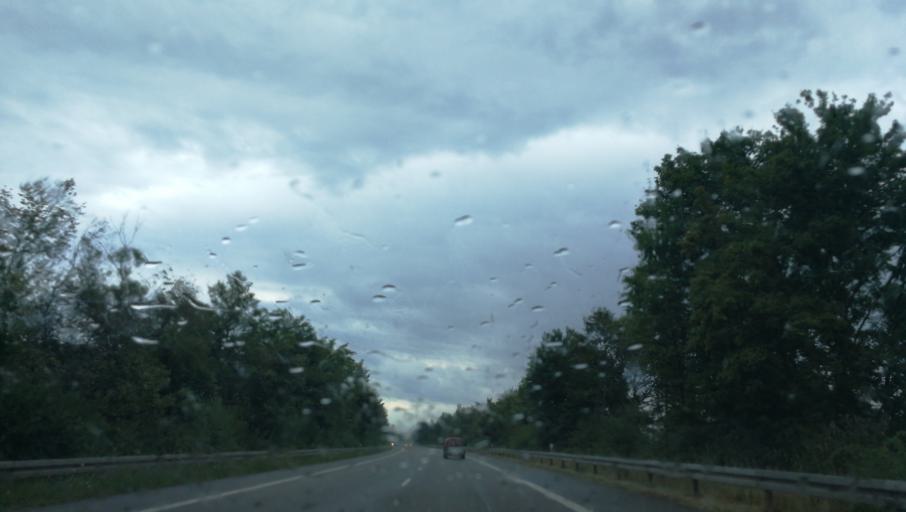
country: DE
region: Saarland
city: Losheim
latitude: 49.5117
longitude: 6.7649
